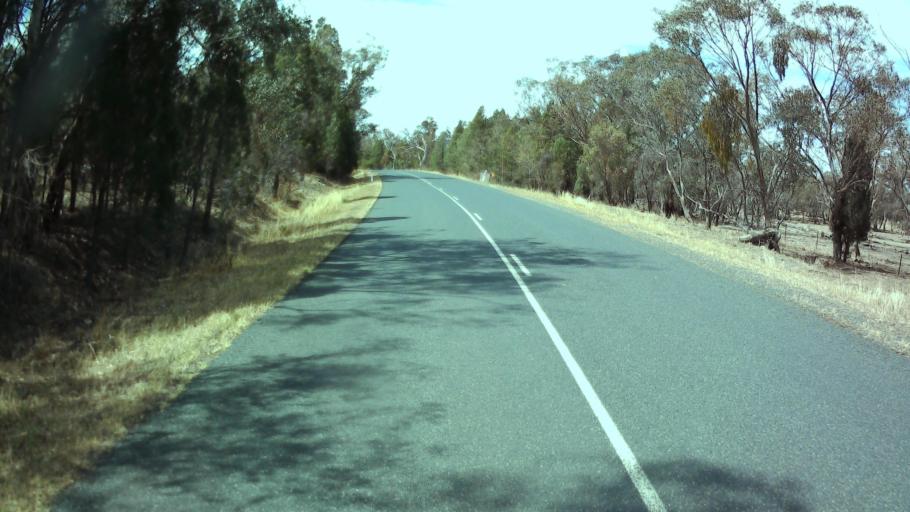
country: AU
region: New South Wales
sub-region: Weddin
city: Grenfell
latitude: -33.6789
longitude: 148.2820
